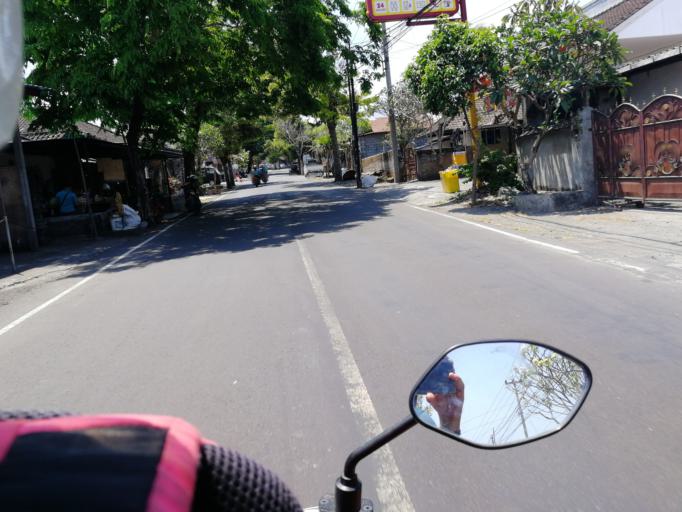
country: ID
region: Bali
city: Subagan
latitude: -8.4510
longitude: 115.5940
